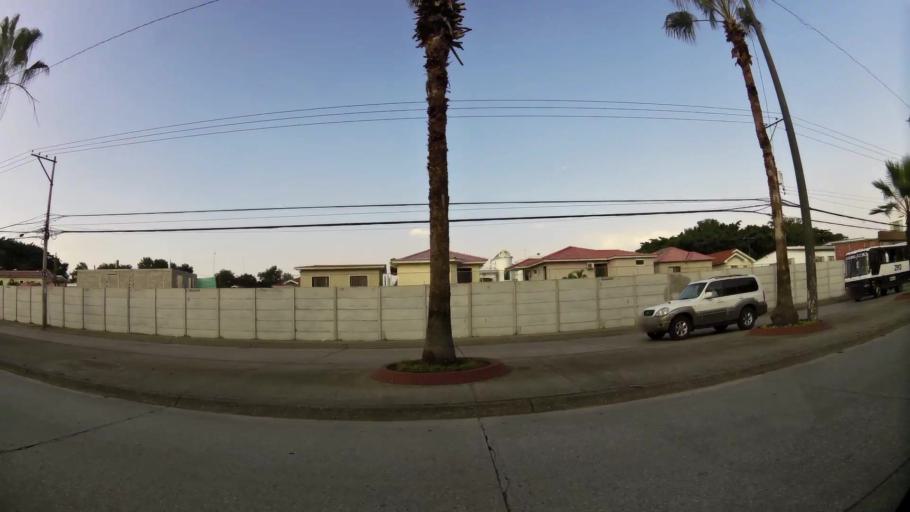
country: EC
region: Guayas
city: Guayaquil
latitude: -2.1524
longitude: -79.9052
